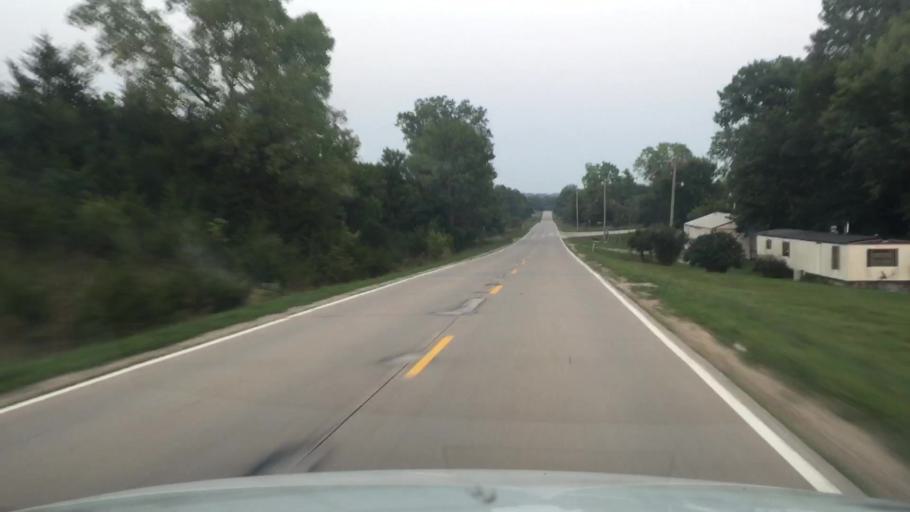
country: US
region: Iowa
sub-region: Warren County
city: Indianola
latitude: 41.1909
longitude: -93.6476
